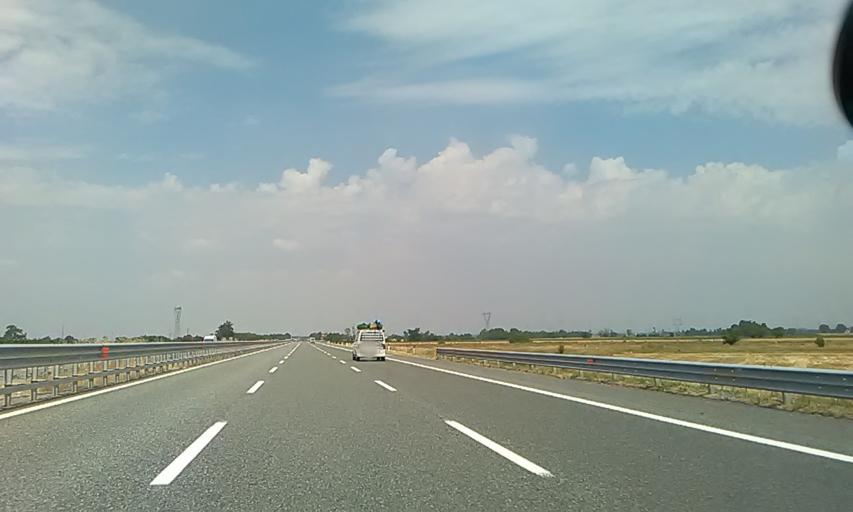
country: IT
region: Piedmont
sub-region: Provincia di Alessandria
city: Castelspina
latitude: 44.7921
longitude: 8.6132
